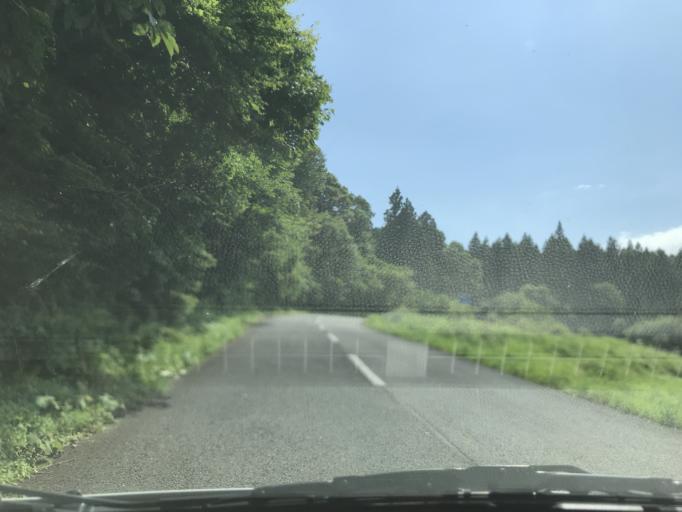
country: JP
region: Iwate
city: Ofunato
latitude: 38.9920
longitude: 141.4281
